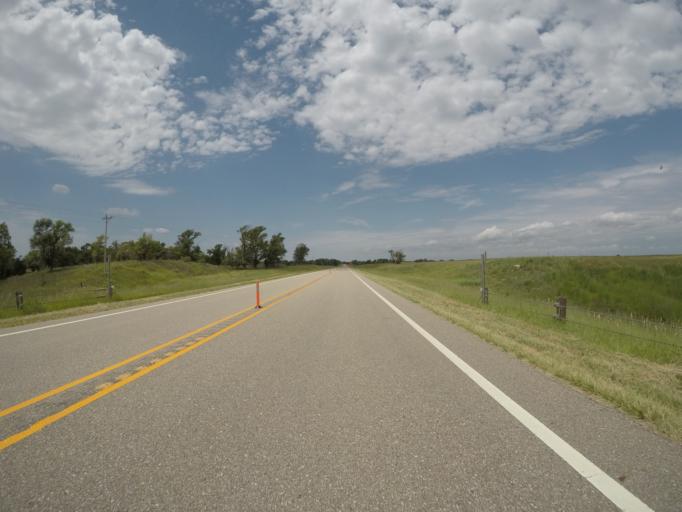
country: US
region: Kansas
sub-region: Graham County
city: Hill City
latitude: 39.3944
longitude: -99.6254
